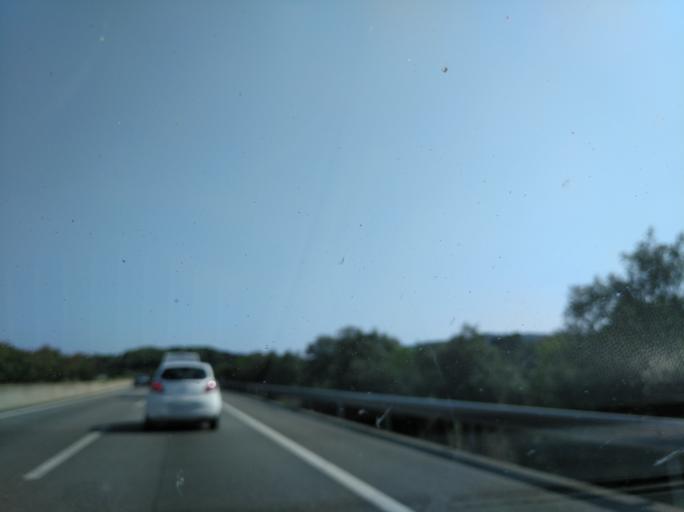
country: ES
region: Catalonia
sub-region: Provincia de Barcelona
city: Argentona
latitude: 41.5645
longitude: 2.3980
